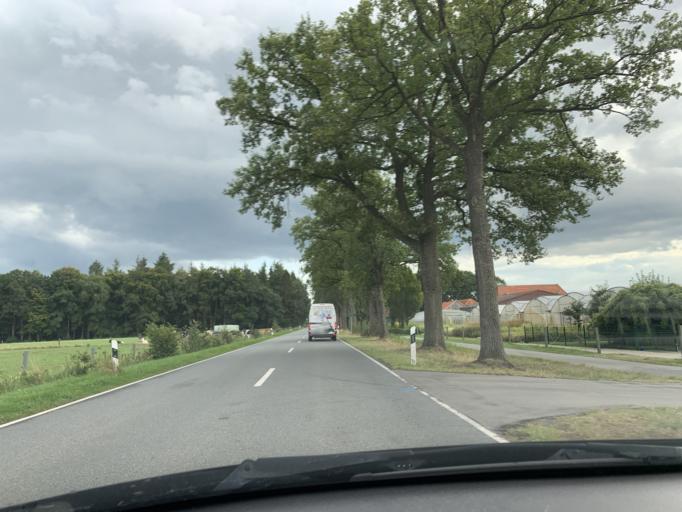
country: DE
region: Lower Saxony
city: Westerstede
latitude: 53.2969
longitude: 7.9185
